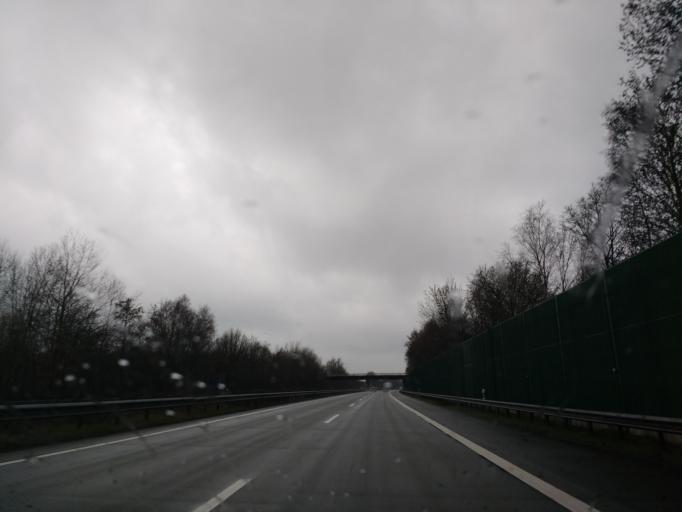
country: DE
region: Lower Saxony
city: Langen
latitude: 53.5977
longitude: 8.6472
